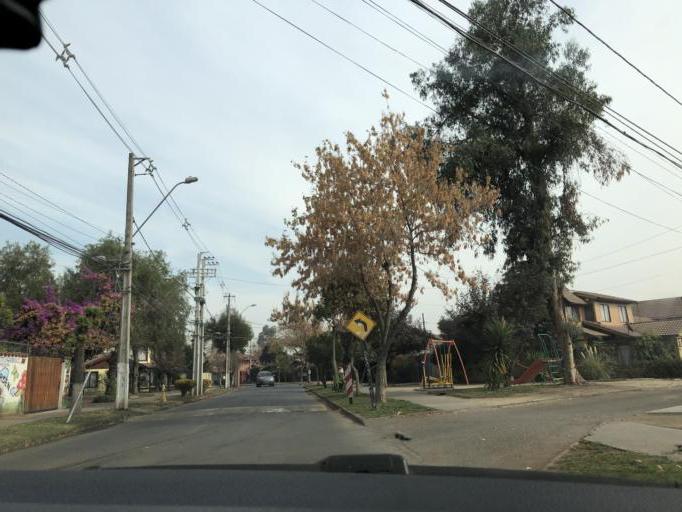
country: CL
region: Santiago Metropolitan
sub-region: Provincia de Cordillera
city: Puente Alto
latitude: -33.5491
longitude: -70.5637
